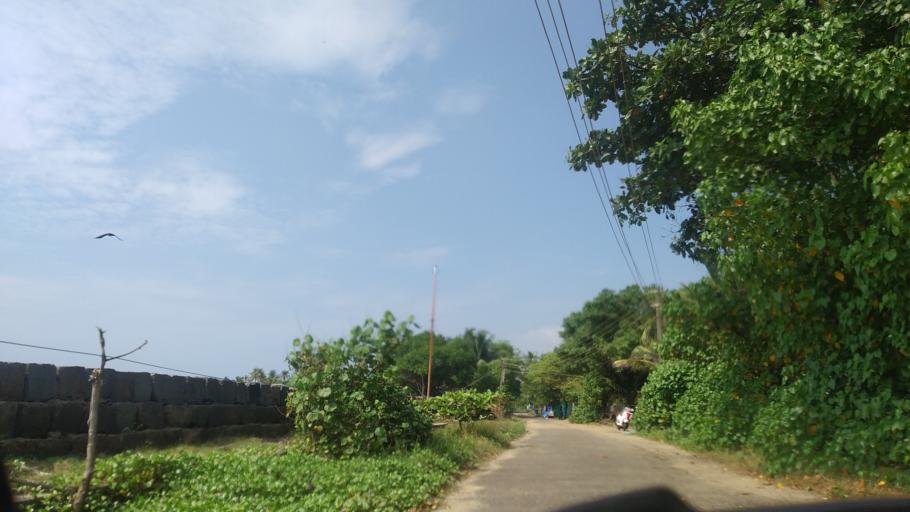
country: IN
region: Kerala
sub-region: Ernakulam
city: Elur
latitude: 10.0500
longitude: 76.2045
